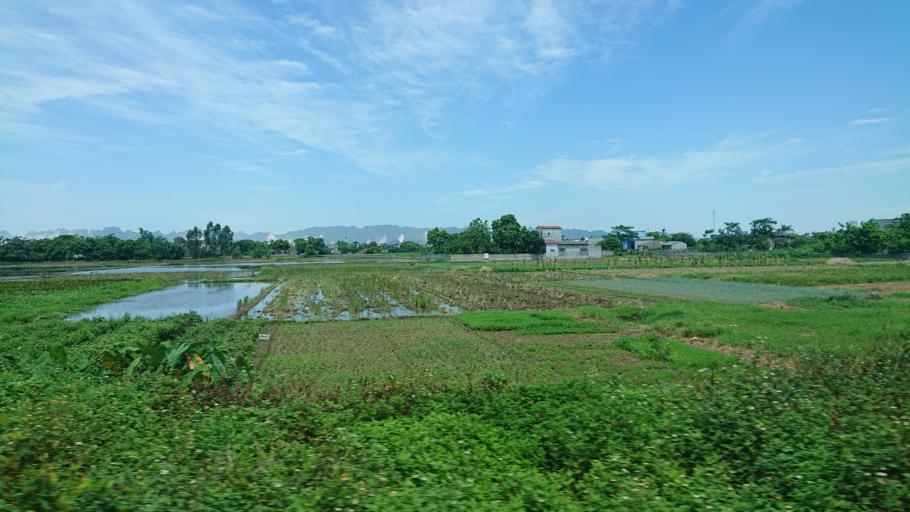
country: VN
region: Ha Nam
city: Thanh Pho Phu Ly
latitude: 20.5278
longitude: 105.9460
